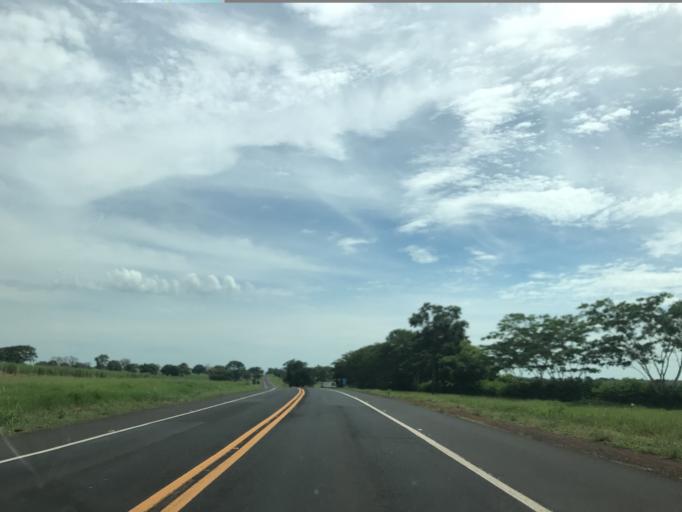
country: BR
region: Sao Paulo
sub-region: Nova Granada
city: Nova Granada
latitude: -20.4062
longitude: -49.2469
